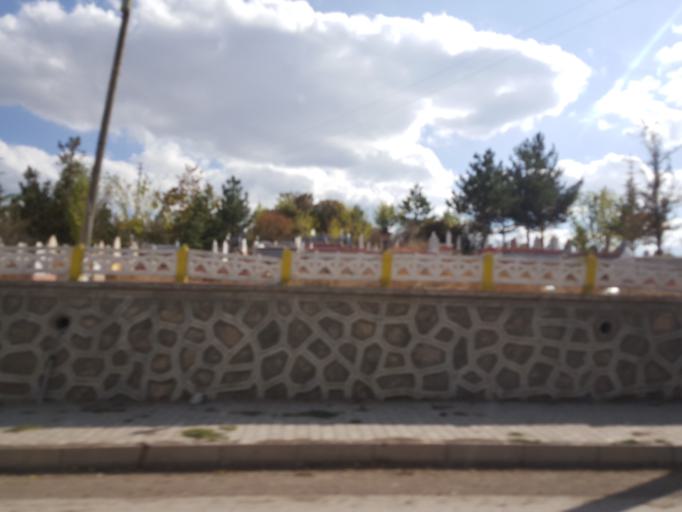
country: TR
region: Tokat
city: Yesilyurt
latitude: 40.0079
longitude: 36.2060
